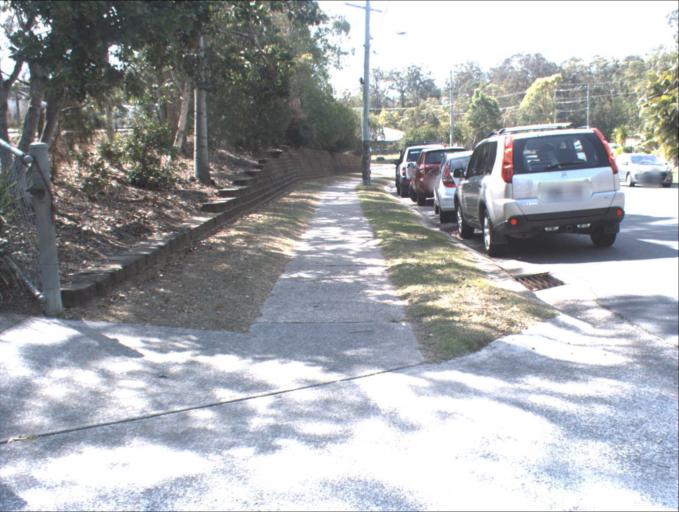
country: AU
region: Queensland
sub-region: Logan
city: Slacks Creek
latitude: -27.6469
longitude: 153.1771
